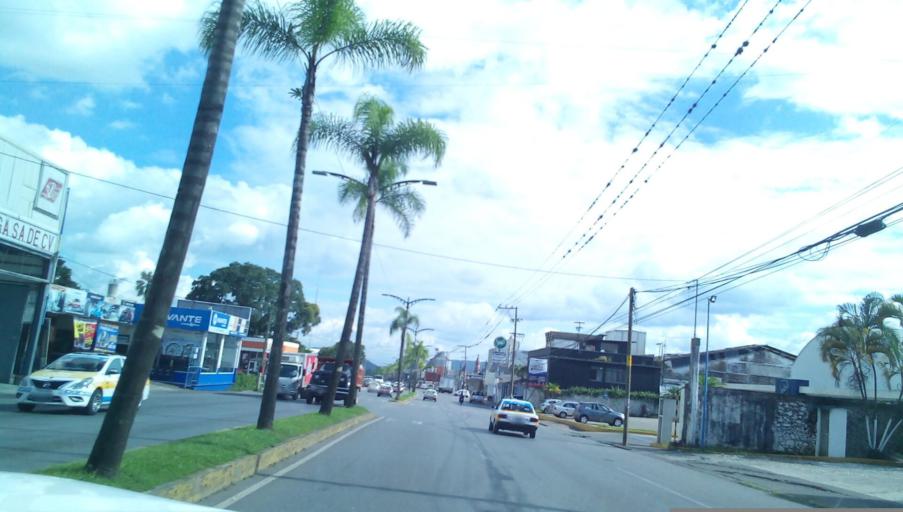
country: MX
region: Veracruz
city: Cordoba
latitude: 18.8788
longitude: -96.9197
